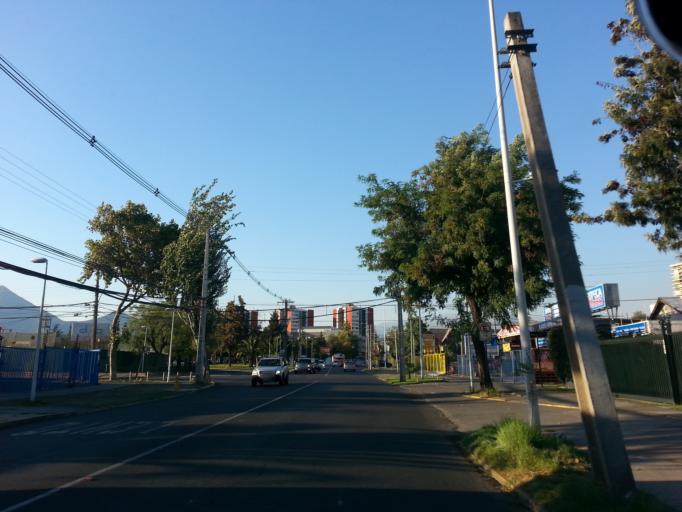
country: CL
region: Santiago Metropolitan
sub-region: Provincia de Santiago
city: Villa Presidente Frei, Nunoa, Santiago, Chile
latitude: -33.4102
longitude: -70.5521
